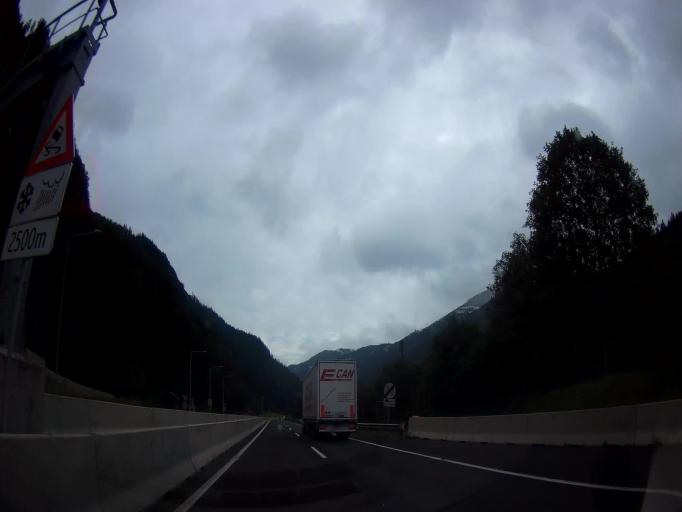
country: AT
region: Styria
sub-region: Politischer Bezirk Leoben
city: Wald am Schoberpass
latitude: 47.4394
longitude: 14.6925
